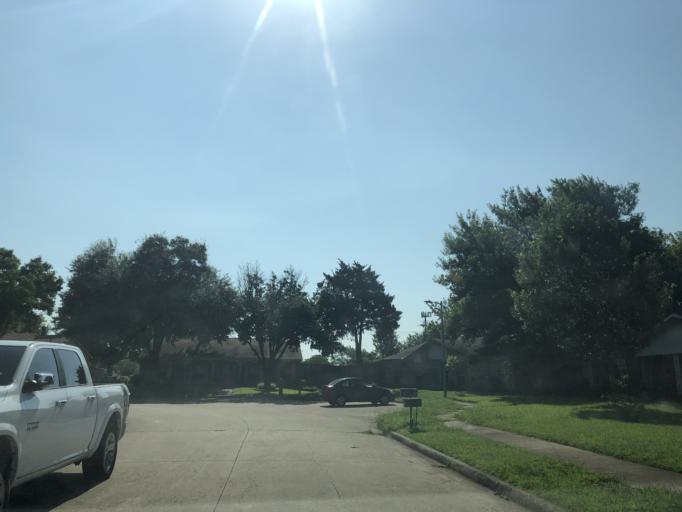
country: US
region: Texas
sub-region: Dallas County
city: Sunnyvale
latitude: 32.8207
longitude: -96.5981
